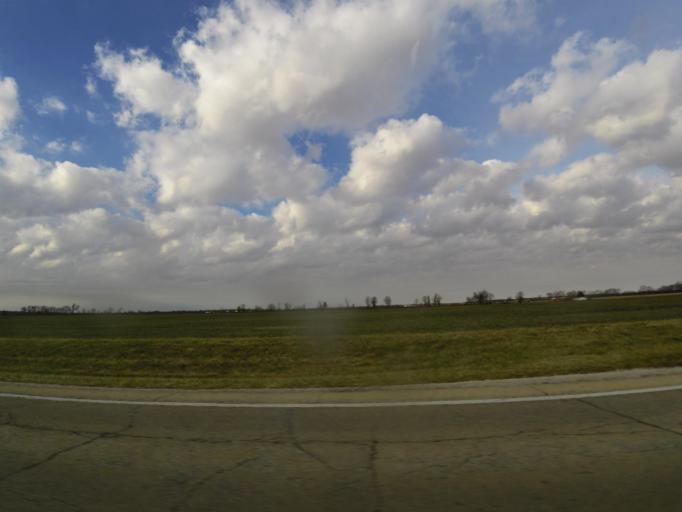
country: US
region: Illinois
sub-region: Fayette County
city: Ramsey
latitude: 39.2143
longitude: -89.1008
